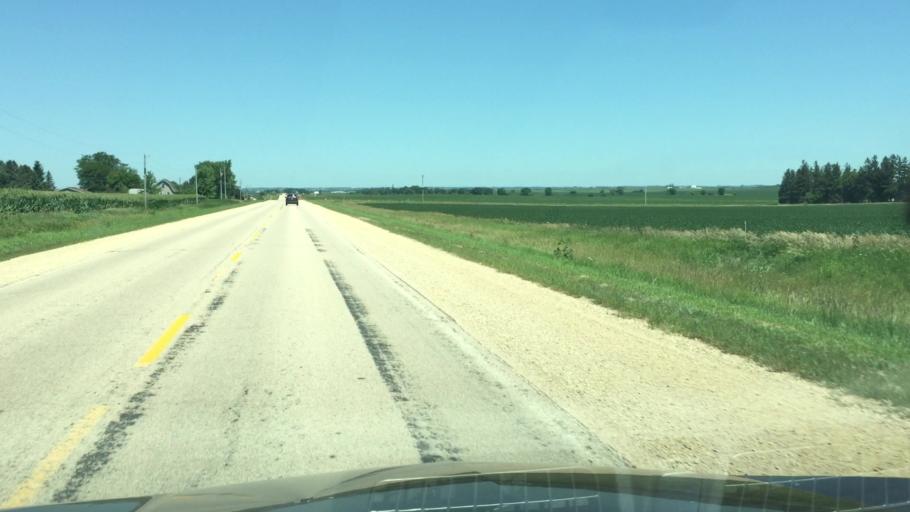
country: US
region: Iowa
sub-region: Cedar County
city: Mechanicsville
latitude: 41.9294
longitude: -91.1518
